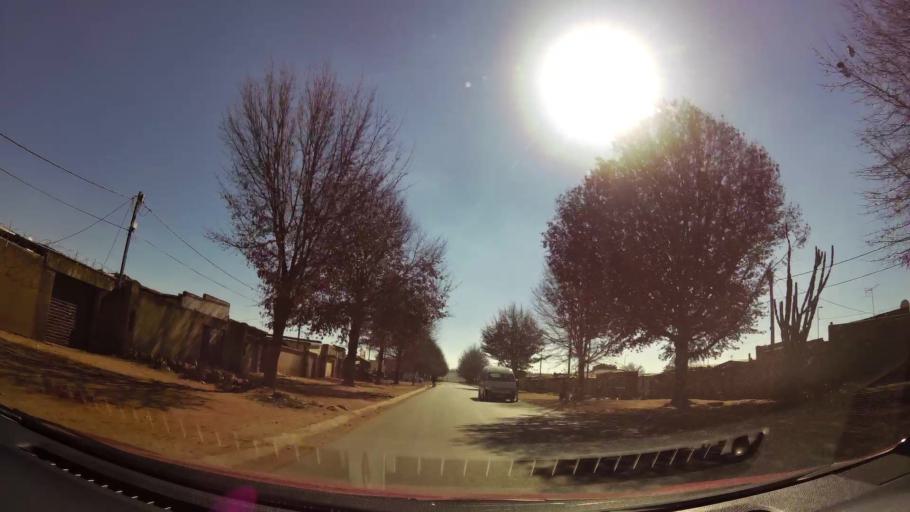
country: ZA
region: Gauteng
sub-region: City of Johannesburg Metropolitan Municipality
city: Soweto
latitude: -26.2184
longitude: 27.8325
